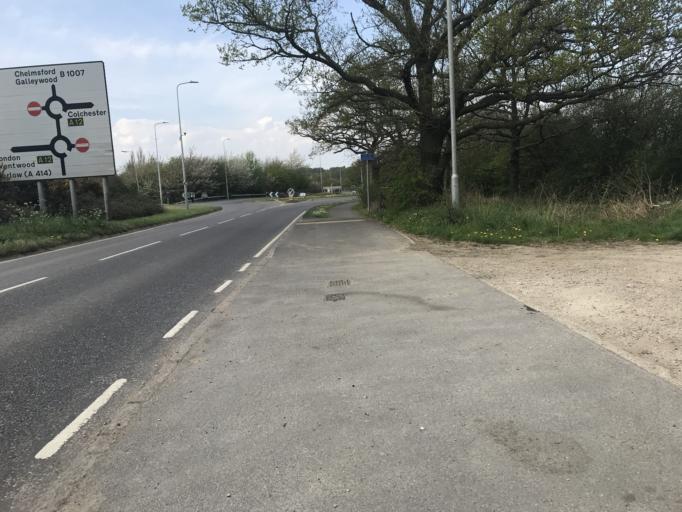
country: GB
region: England
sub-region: Essex
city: Stock
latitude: 51.6858
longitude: 0.4658
